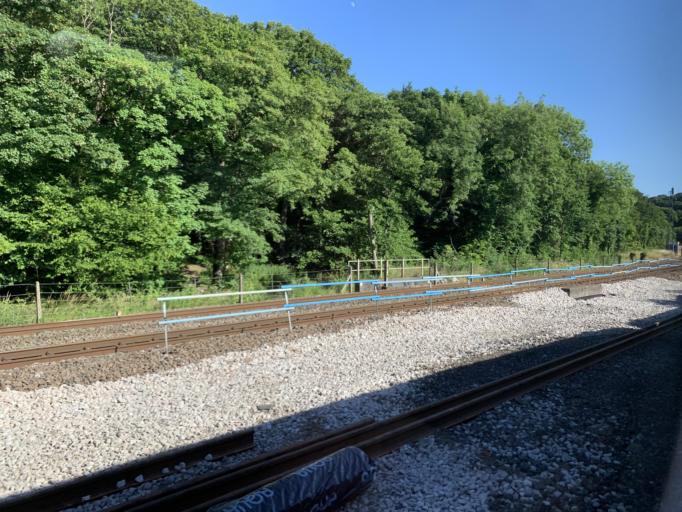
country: GB
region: England
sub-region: Derbyshire
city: Dronfield
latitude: 53.3296
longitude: -1.5149
